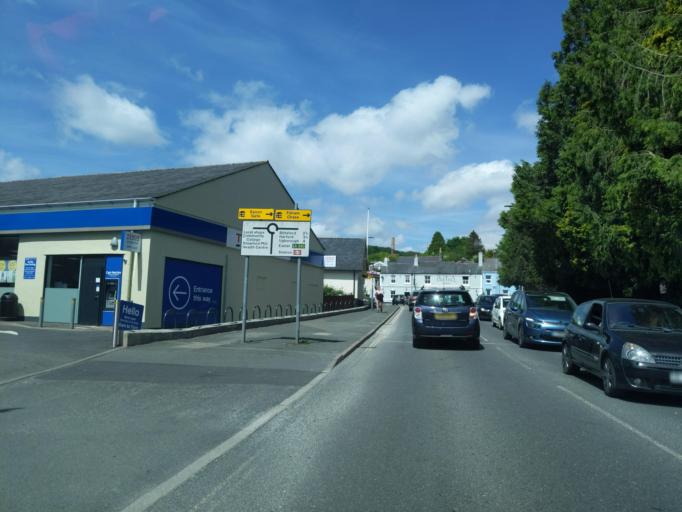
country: GB
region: England
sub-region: Devon
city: Ivybridge
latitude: 50.3897
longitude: -3.9188
